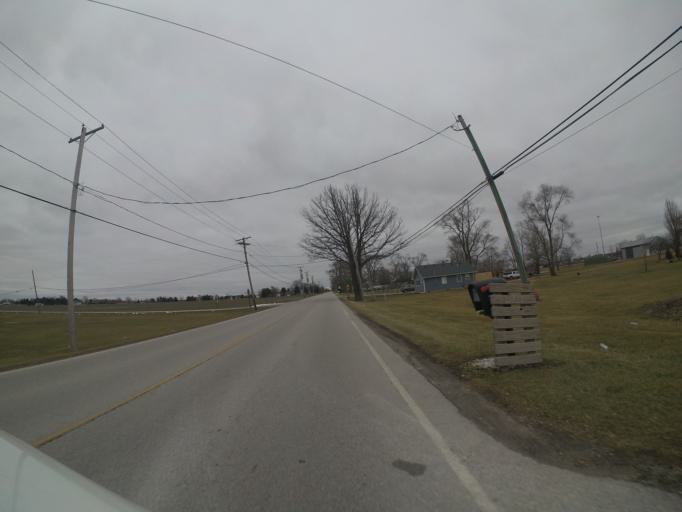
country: US
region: Ohio
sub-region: Wood County
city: Walbridge
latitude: 41.5774
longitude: -83.5123
